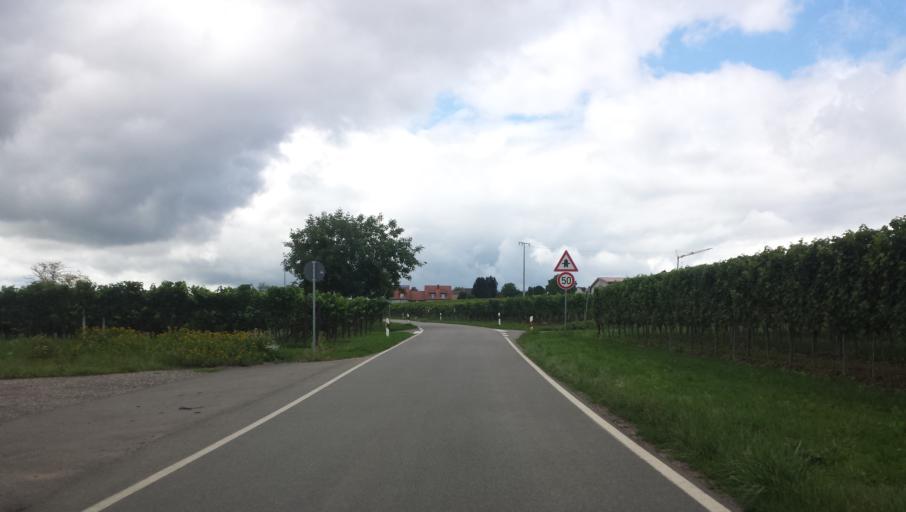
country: DE
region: Rheinland-Pfalz
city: Walsheim
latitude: 49.2224
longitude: 8.1164
